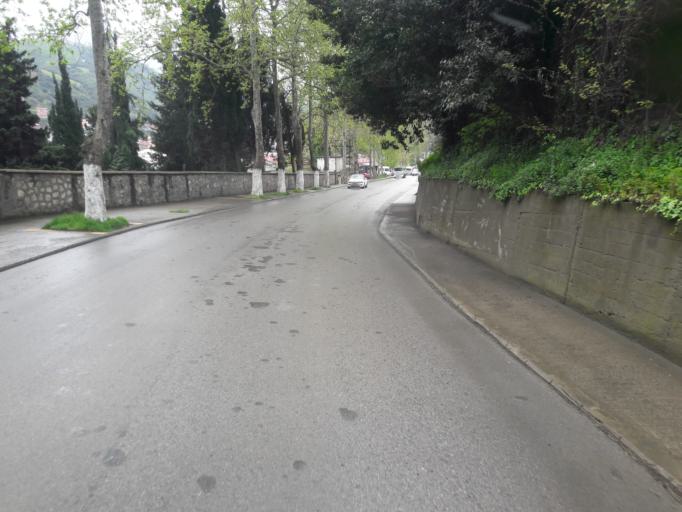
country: TR
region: Trabzon
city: Trabzon
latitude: 40.9938
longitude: 39.7496
